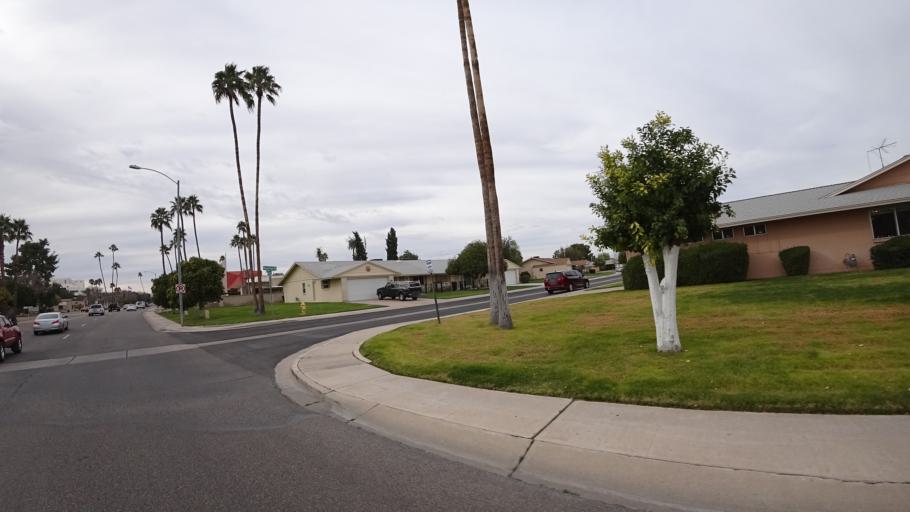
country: US
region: Arizona
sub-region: Maricopa County
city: Sun City
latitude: 33.6051
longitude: -112.2788
